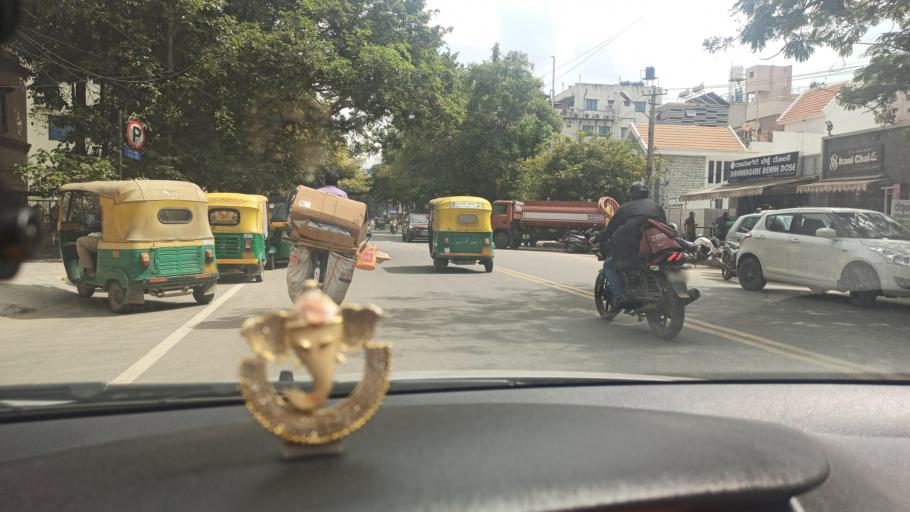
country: IN
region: Karnataka
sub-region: Bangalore Urban
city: Bangalore
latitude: 12.9125
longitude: 77.6338
